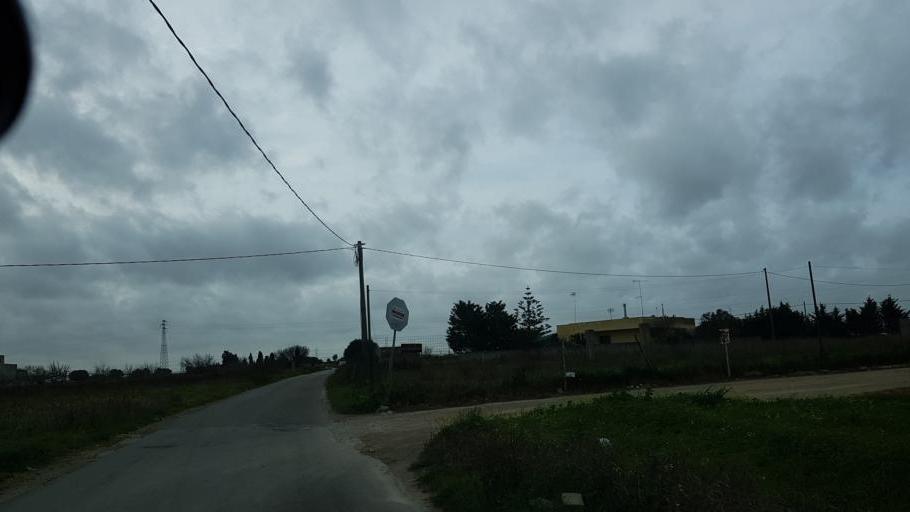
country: IT
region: Apulia
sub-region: Provincia di Brindisi
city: Brindisi
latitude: 40.6123
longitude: 17.9271
